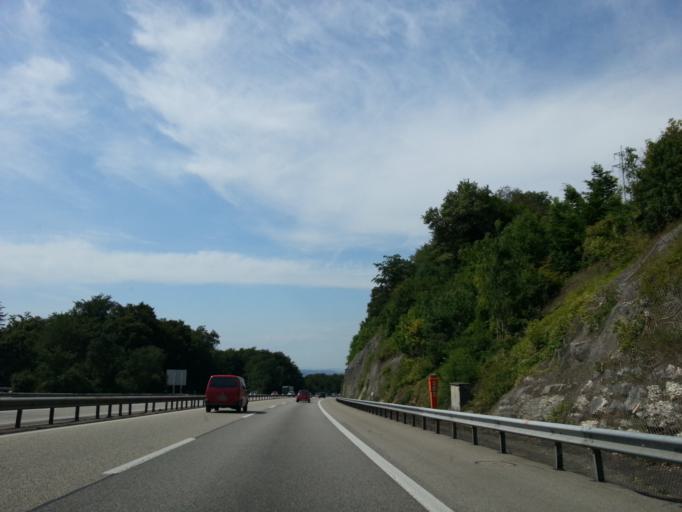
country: CH
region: Solothurn
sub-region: Bezirk Olten
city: Hagendorf
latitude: 47.3365
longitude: 7.8289
